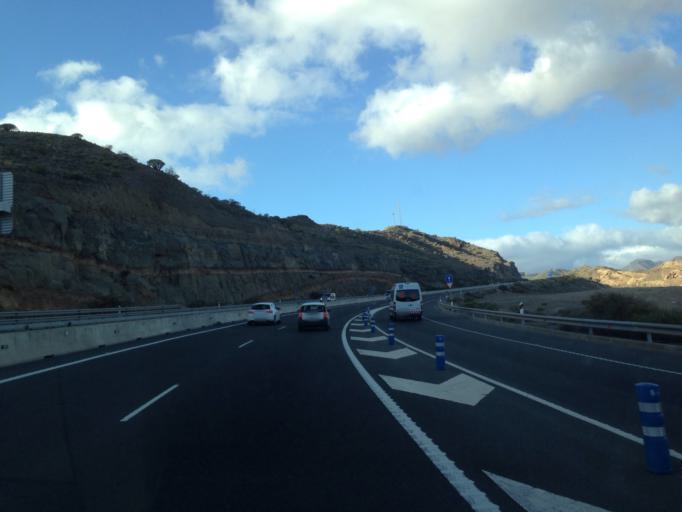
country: ES
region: Canary Islands
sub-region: Provincia de Las Palmas
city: Puerto Rico
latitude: 27.7672
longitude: -15.6743
